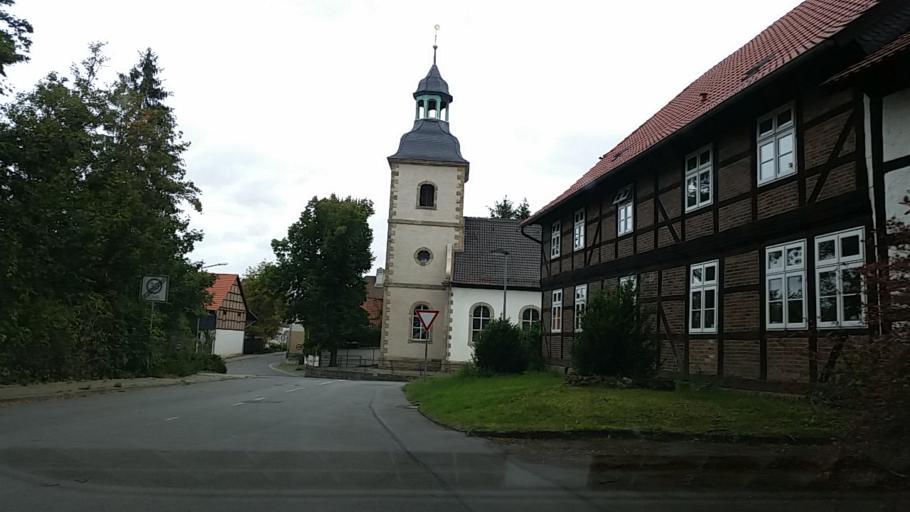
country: DE
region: Lower Saxony
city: Vienenburg
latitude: 51.9471
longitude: 10.5648
